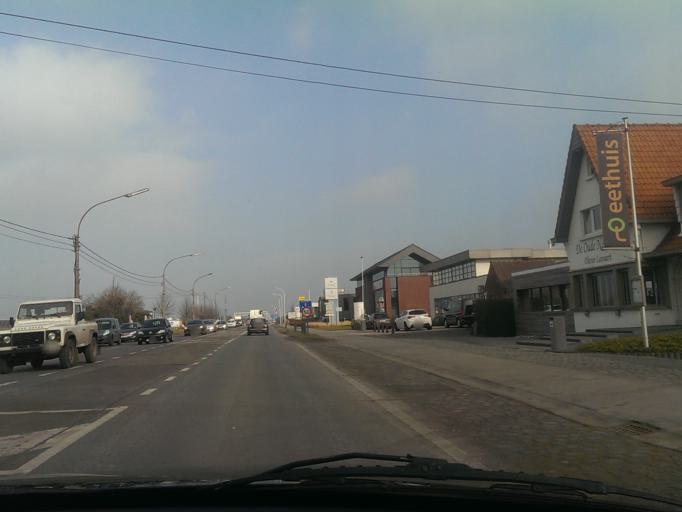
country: BE
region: Flanders
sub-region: Provincie West-Vlaanderen
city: Roeselare
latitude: 50.9226
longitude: 3.1176
